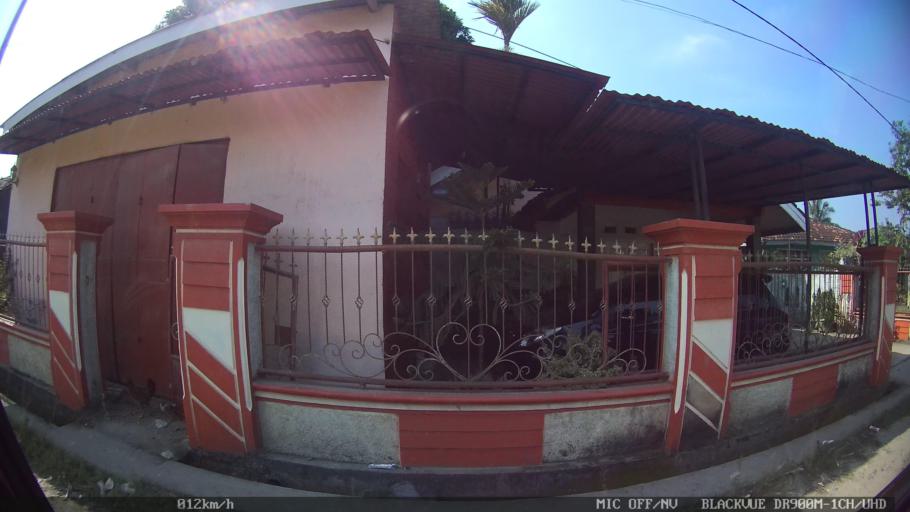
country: ID
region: Lampung
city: Natar
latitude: -5.2569
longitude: 105.1848
